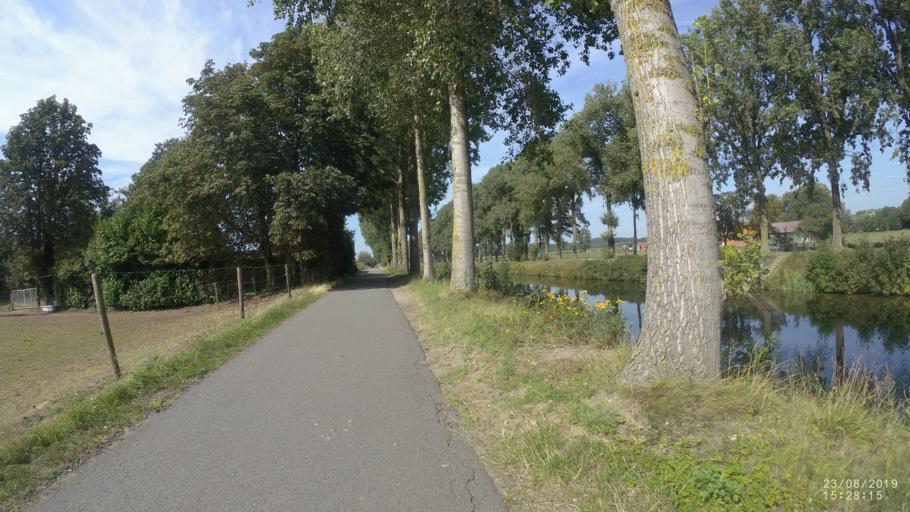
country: BE
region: Flanders
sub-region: Provincie Oost-Vlaanderen
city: Zomergem
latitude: 51.1415
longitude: 3.5573
